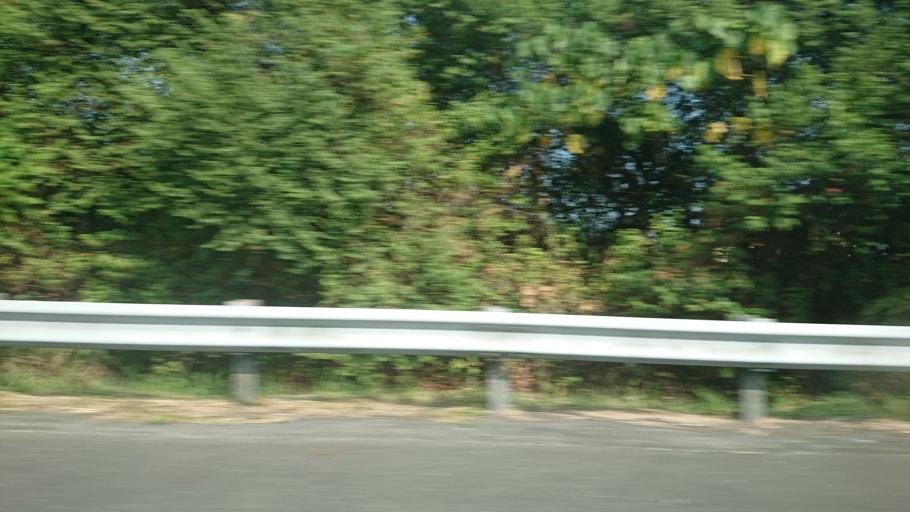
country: TW
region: Taiwan
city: Lugu
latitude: 23.7773
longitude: 120.6913
